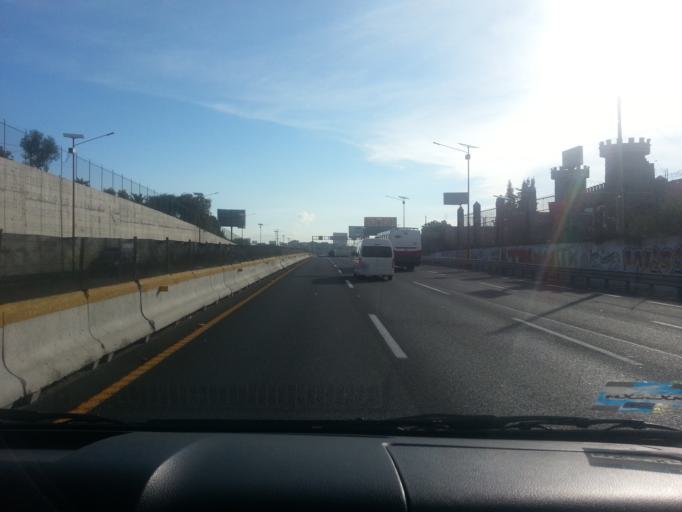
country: MX
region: Mexico
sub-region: Tlalnepantla de Baz
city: Puerto Escondido (Tepeolulco Puerto Escondido)
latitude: 19.5522
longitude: -99.0649
